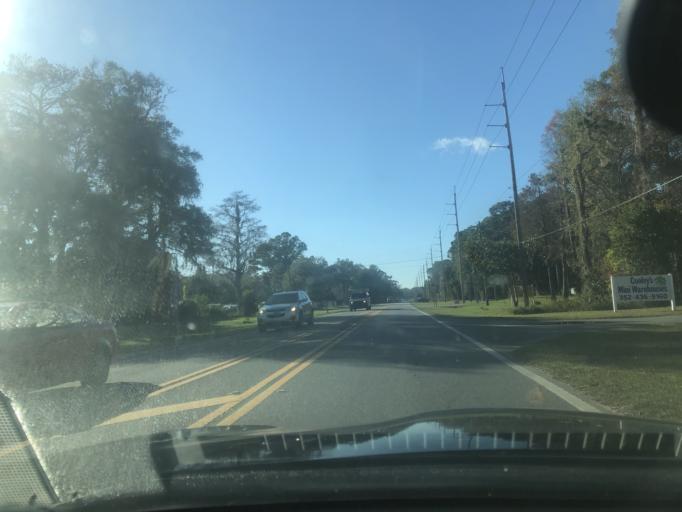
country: US
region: Florida
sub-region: Citrus County
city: Homosassa Springs
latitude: 28.8038
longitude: -82.5689
